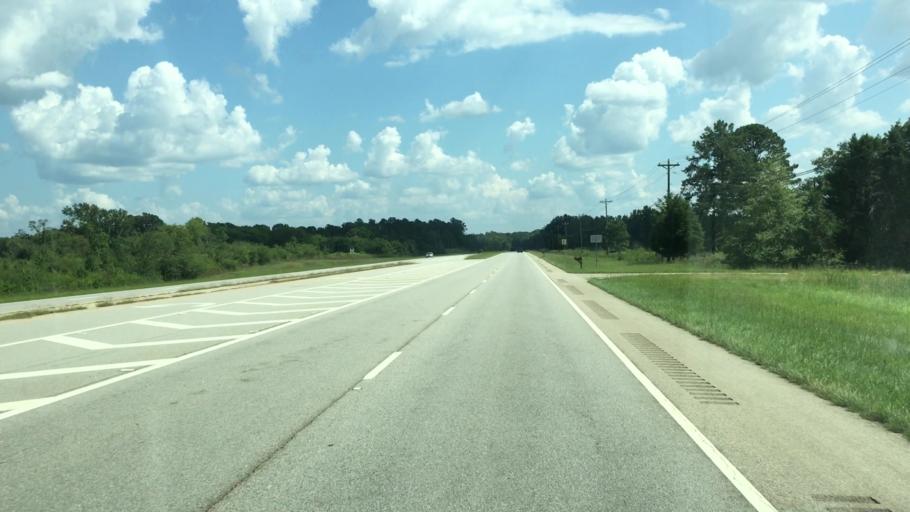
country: US
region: Georgia
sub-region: Putnam County
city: Eatonton
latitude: 33.2504
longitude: -83.3271
